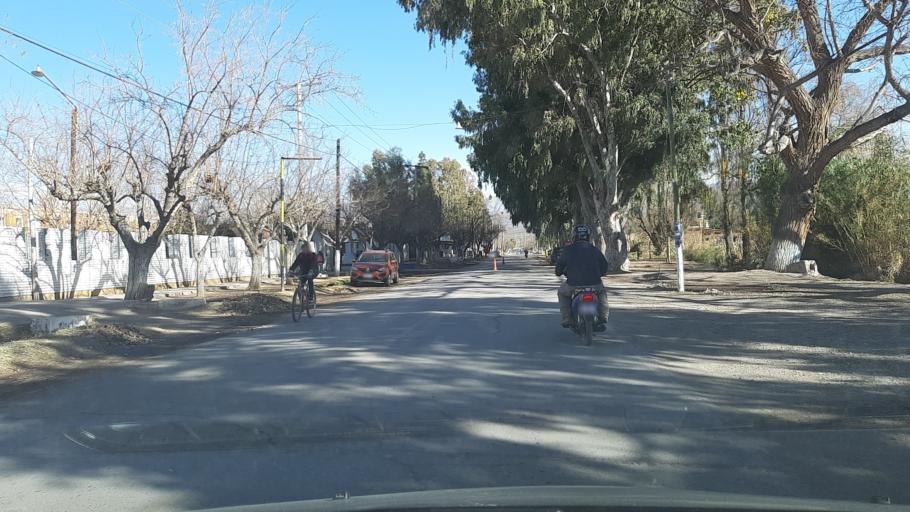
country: AR
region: San Juan
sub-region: Departamento de Zonda
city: Zonda
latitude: -31.4615
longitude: -68.7361
